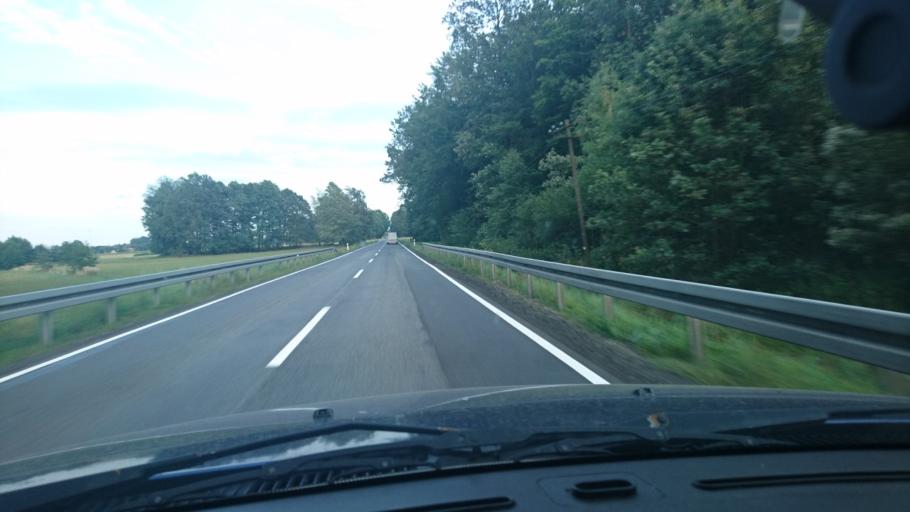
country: PL
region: Opole Voivodeship
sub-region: Powiat oleski
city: Olesno
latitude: 50.8481
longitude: 18.4771
